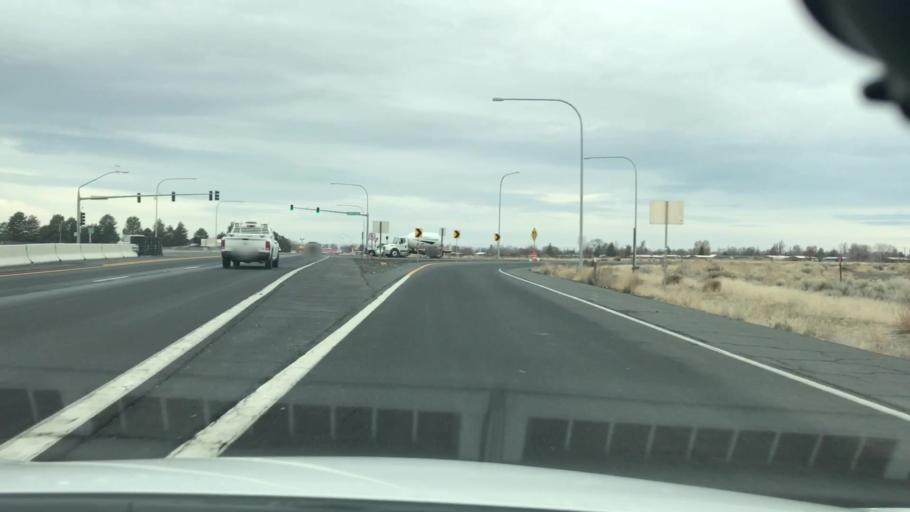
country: US
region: Washington
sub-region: Grant County
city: Cascade Valley
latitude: 47.1564
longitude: -119.3106
